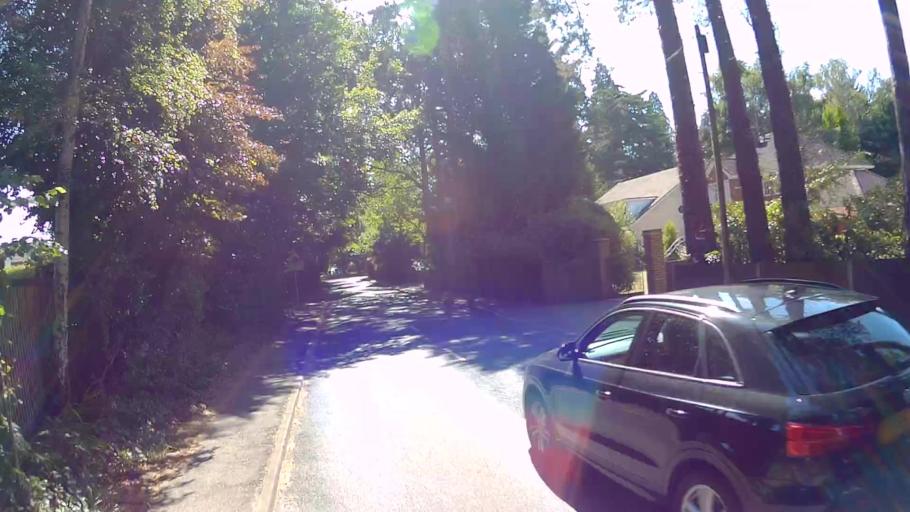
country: GB
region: England
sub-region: Hampshire
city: Yateley
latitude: 51.3678
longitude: -0.8228
